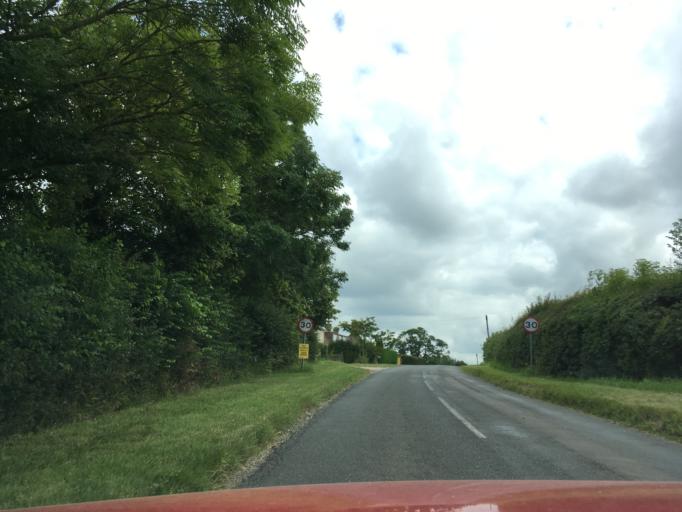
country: GB
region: England
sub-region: Oxfordshire
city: Shipton under Wychwood
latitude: 51.8925
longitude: -1.6430
